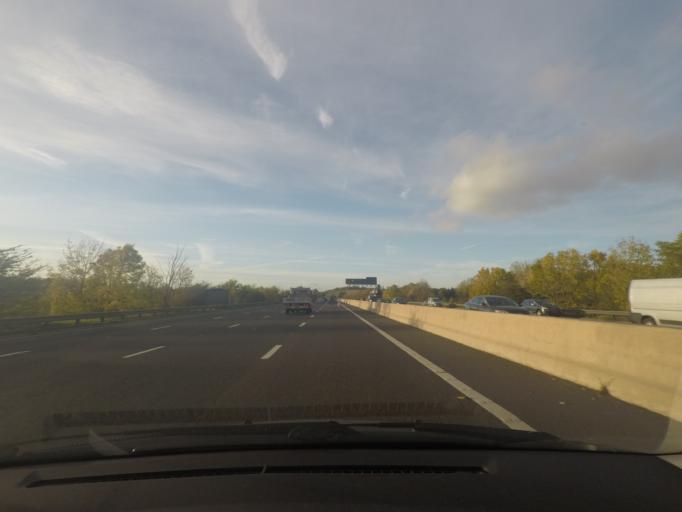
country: GB
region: England
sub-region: City and Borough of Wakefield
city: Crigglestone
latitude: 53.6607
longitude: -1.5333
